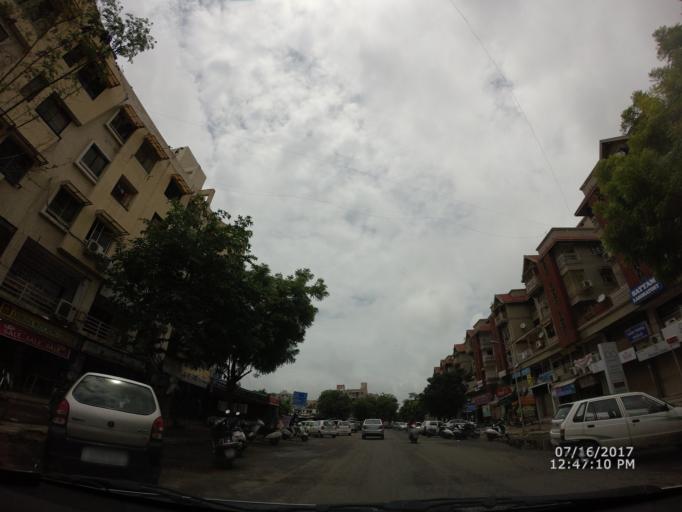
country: IN
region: Gujarat
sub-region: Ahmadabad
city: Sarkhej
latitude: 23.0185
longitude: 72.5143
